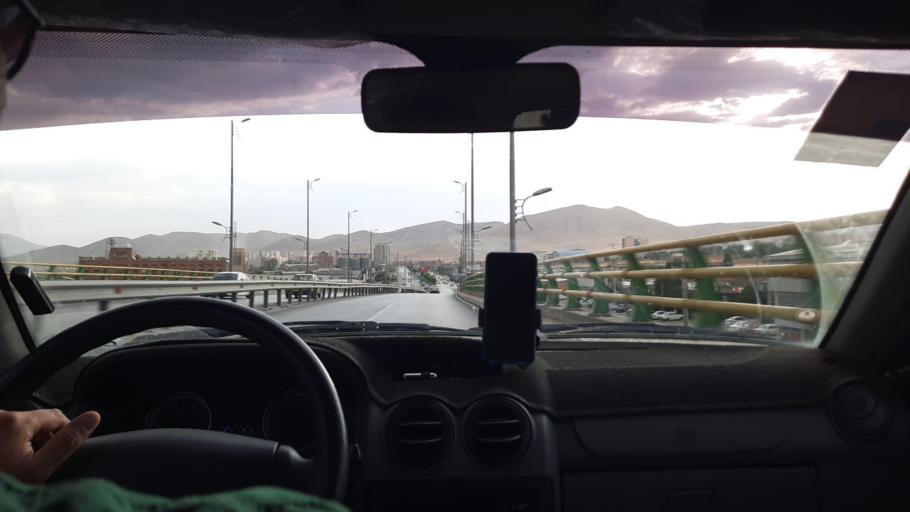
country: IR
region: Markazi
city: Arak
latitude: 34.0770
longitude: 49.6448
